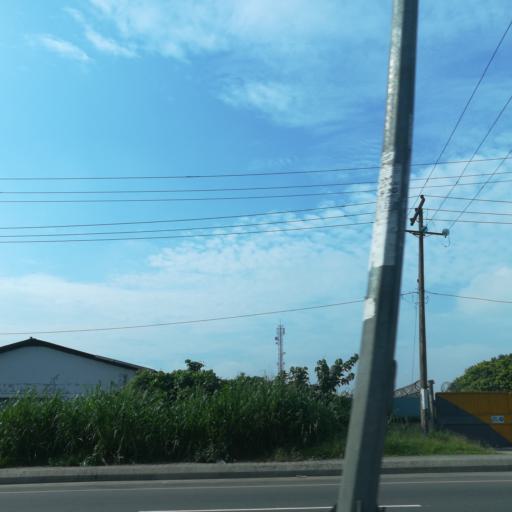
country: NG
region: Rivers
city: Port Harcourt
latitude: 4.8070
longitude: 7.0242
